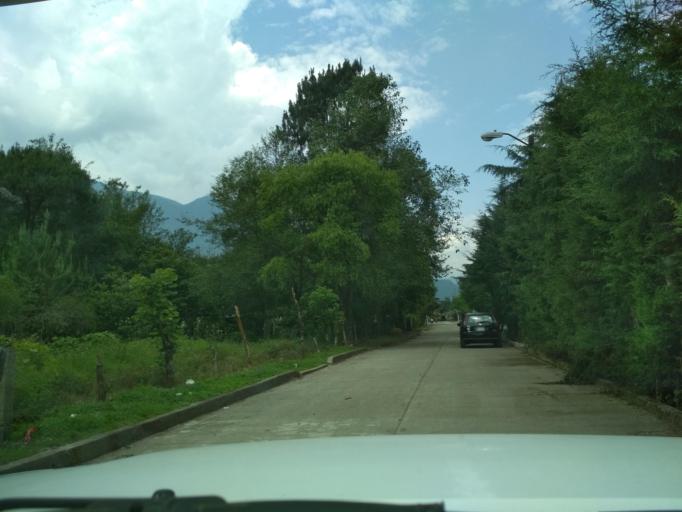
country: MX
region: Veracruz
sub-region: Mariano Escobedo
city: Mariano Escobedo
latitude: 18.9129
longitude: -97.1259
